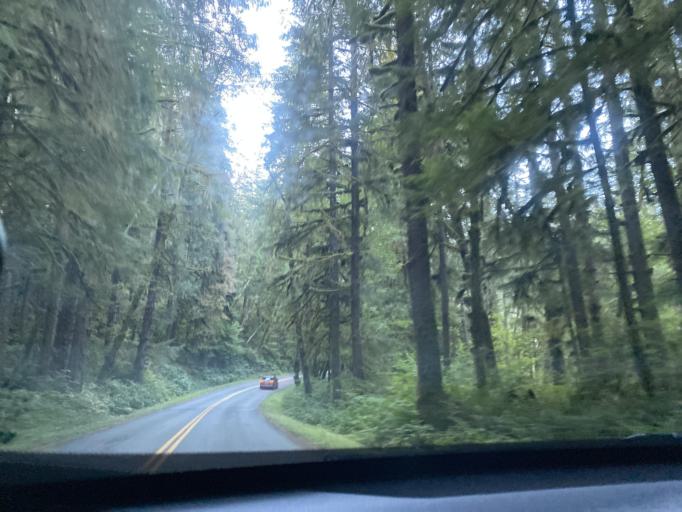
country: US
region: Washington
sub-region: Clallam County
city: Forks
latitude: 47.8132
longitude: -124.1047
